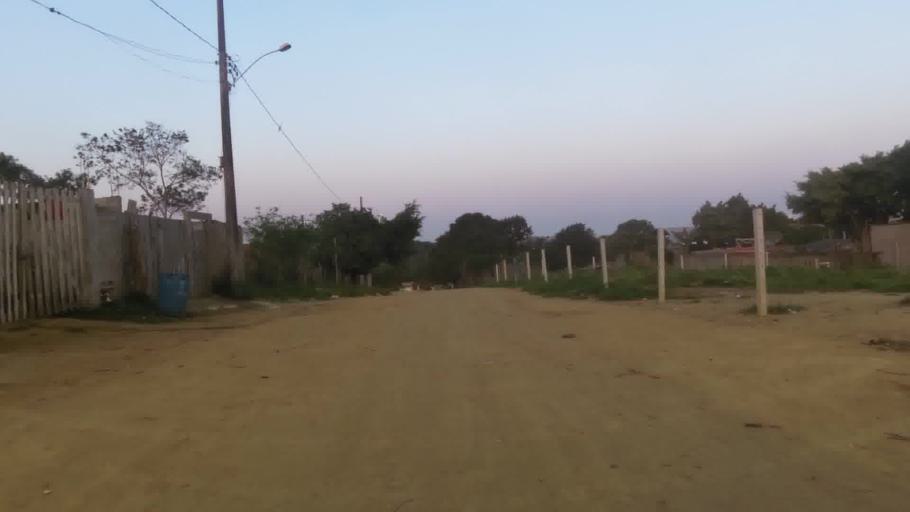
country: BR
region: Espirito Santo
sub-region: Piuma
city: Piuma
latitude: -20.8265
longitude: -40.7216
